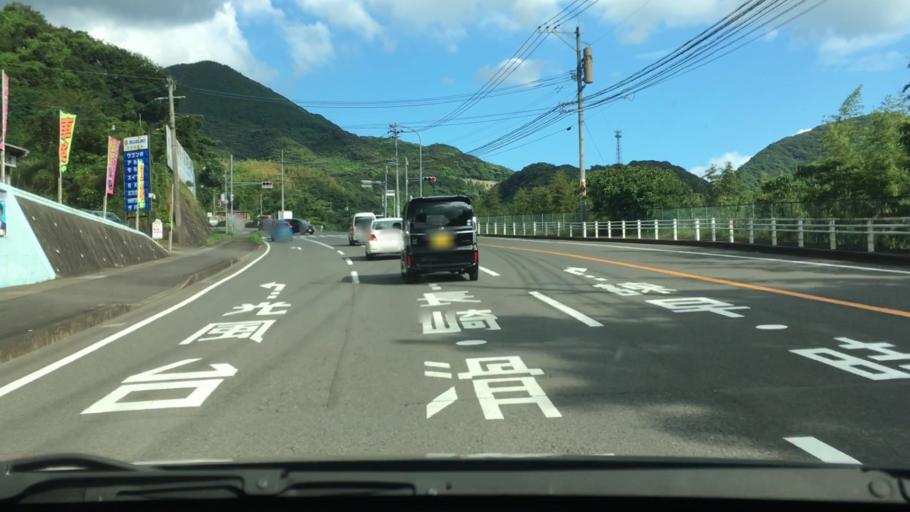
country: JP
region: Nagasaki
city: Togitsu
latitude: 32.8180
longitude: 129.8031
